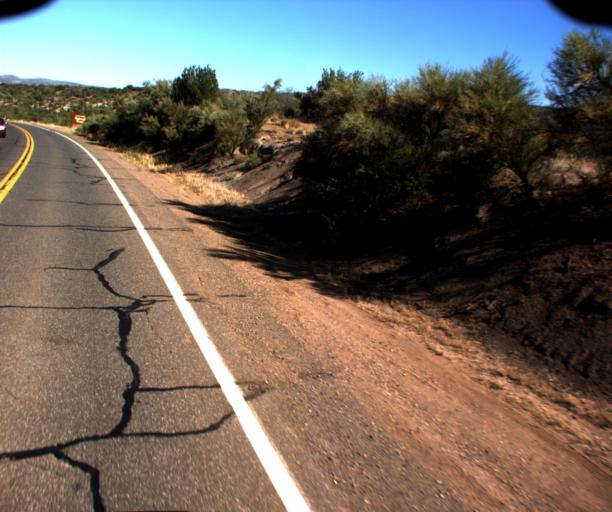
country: US
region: Arizona
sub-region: Yavapai County
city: Lake Montezuma
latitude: 34.6940
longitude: -111.7527
